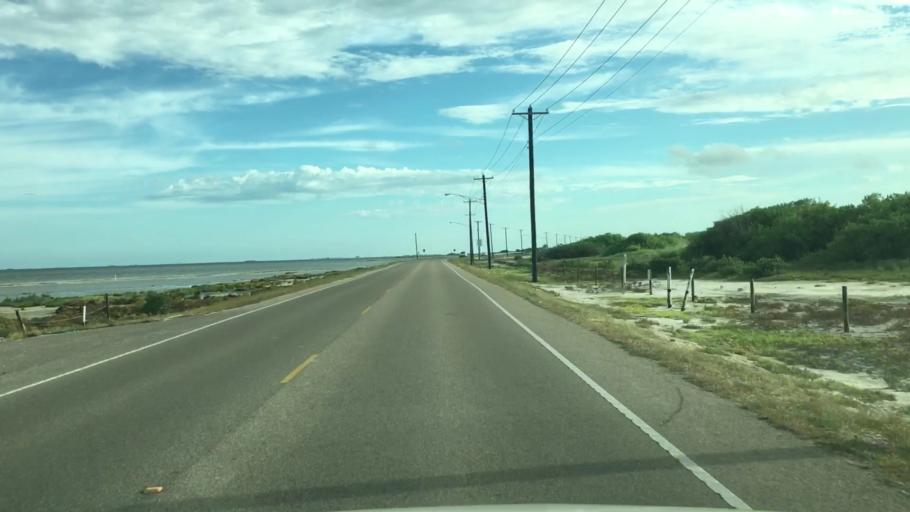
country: US
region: Texas
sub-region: Nueces County
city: Corpus Christi
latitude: 27.6555
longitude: -97.2780
